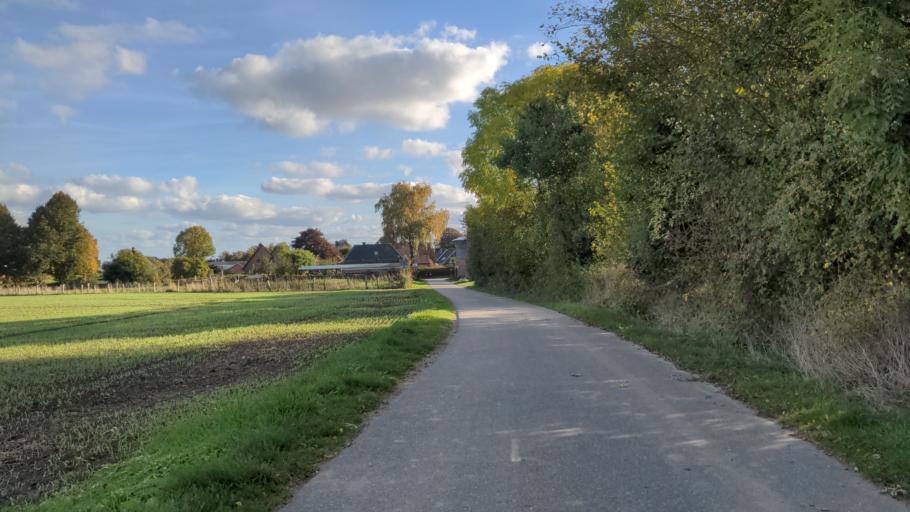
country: DE
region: Schleswig-Holstein
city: Schashagen
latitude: 54.1339
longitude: 10.9080
